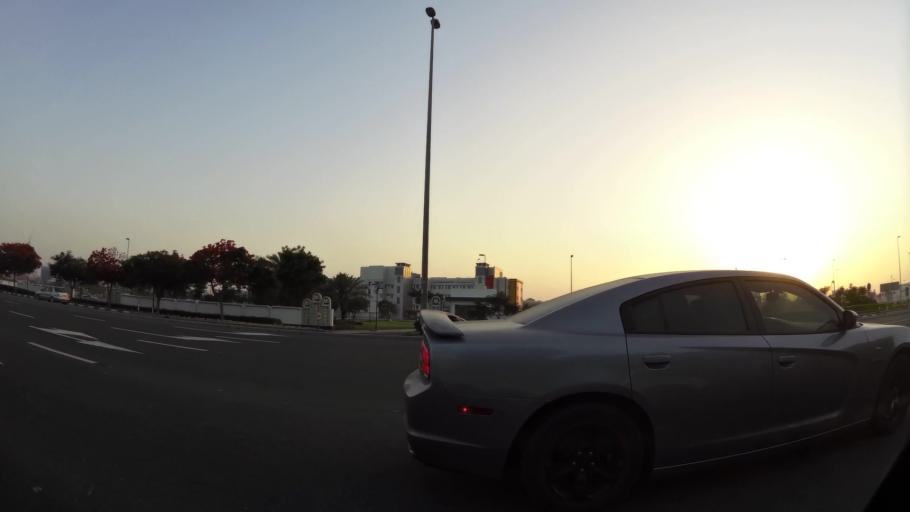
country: AE
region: Ash Shariqah
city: Sharjah
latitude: 25.2450
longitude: 55.3224
